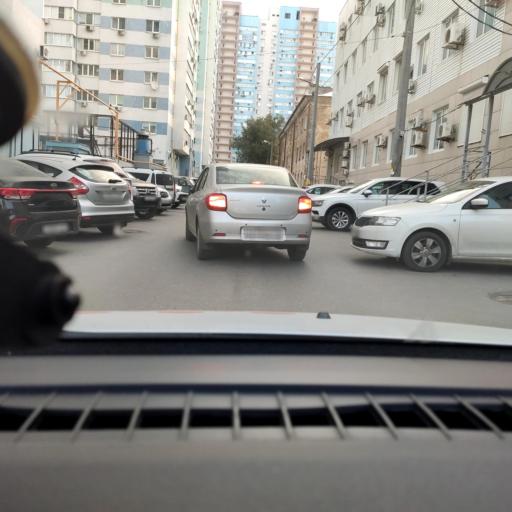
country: RU
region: Samara
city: Samara
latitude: 53.2206
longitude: 50.1938
